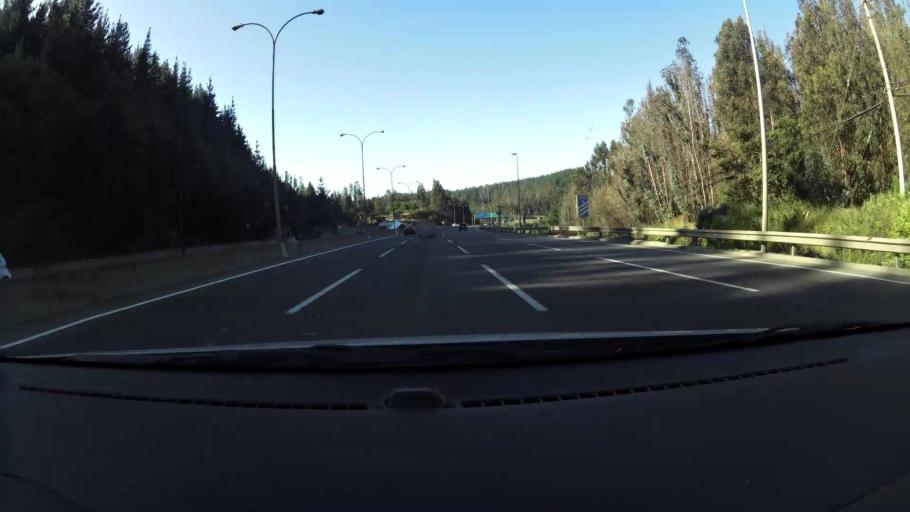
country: CL
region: Valparaiso
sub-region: Provincia de Valparaiso
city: Vina del Mar
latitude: -33.1015
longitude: -71.5481
